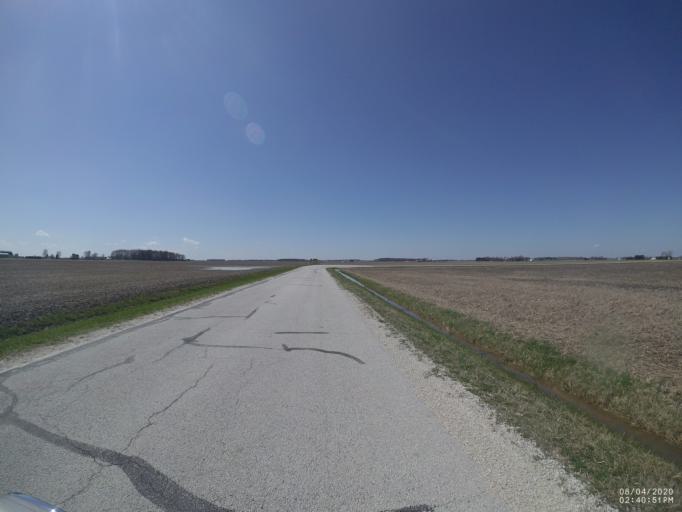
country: US
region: Ohio
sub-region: Sandusky County
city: Gibsonburg
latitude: 41.2833
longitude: -83.2959
